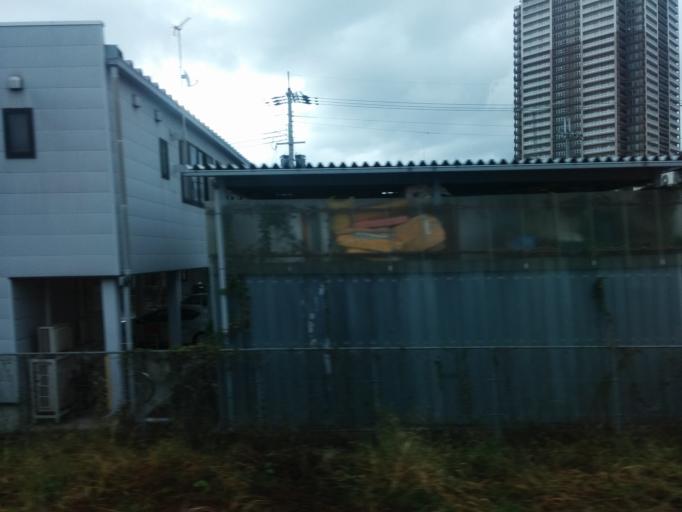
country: JP
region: Shiga Prefecture
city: Kusatsu
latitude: 35.0388
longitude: 135.9817
